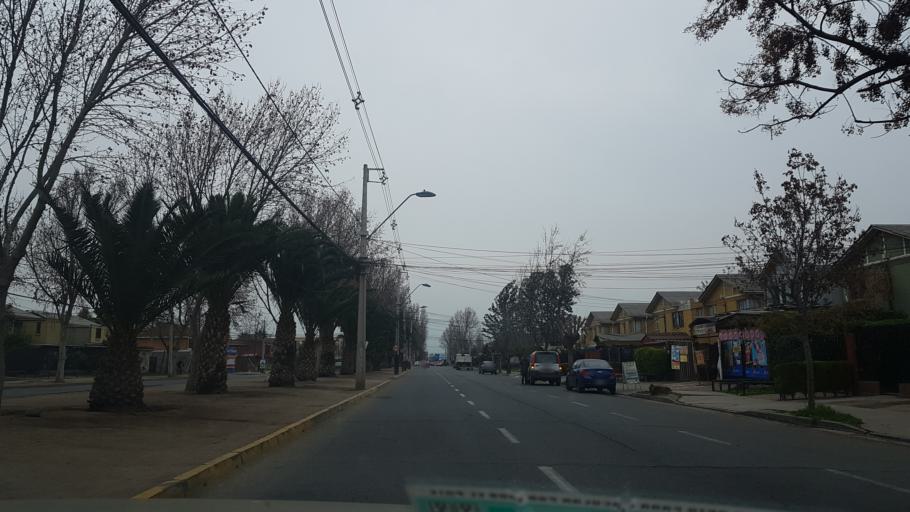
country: CL
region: Santiago Metropolitan
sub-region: Provincia de Santiago
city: Lo Prado
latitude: -33.3569
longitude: -70.7171
